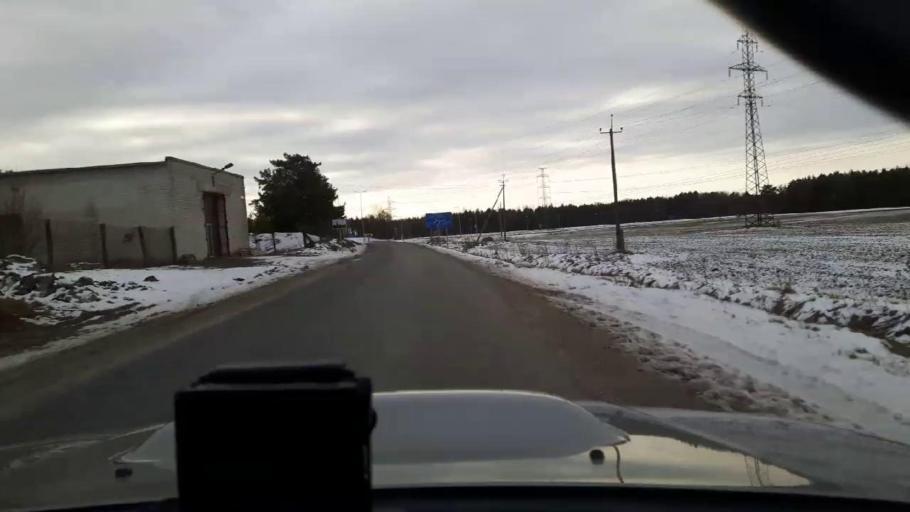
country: EE
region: Harju
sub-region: Saue vald
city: Laagri
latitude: 59.3485
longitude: 24.5993
